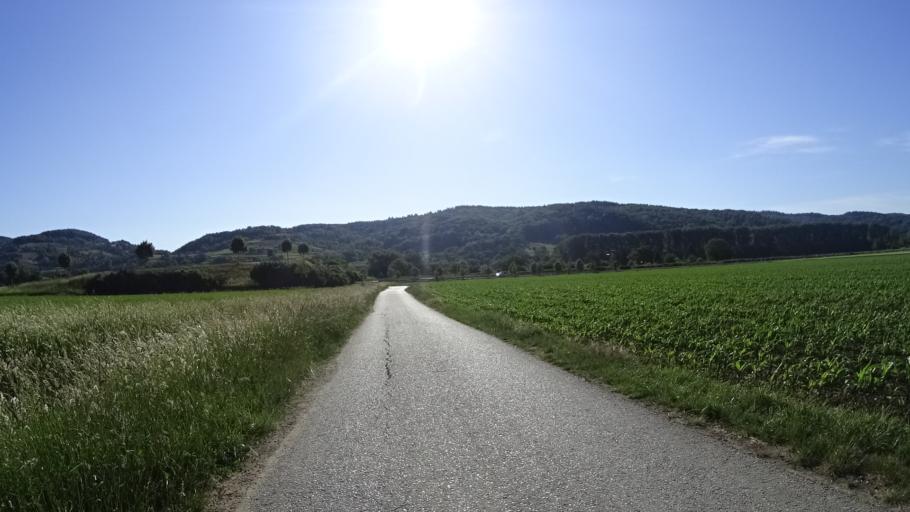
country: DE
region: Baden-Wuerttemberg
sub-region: Karlsruhe Region
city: Hemsbach
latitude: 49.6033
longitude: 8.6430
